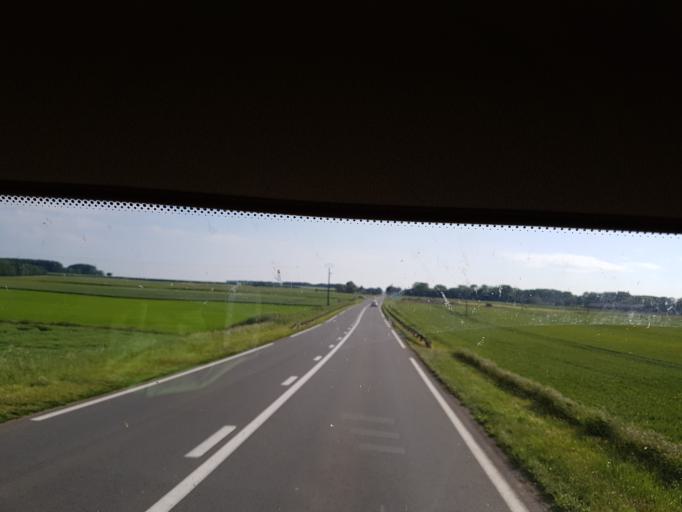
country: FR
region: Picardie
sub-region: Departement de la Somme
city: Crecy-en-Ponthieu
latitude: 50.2327
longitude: 1.9389
